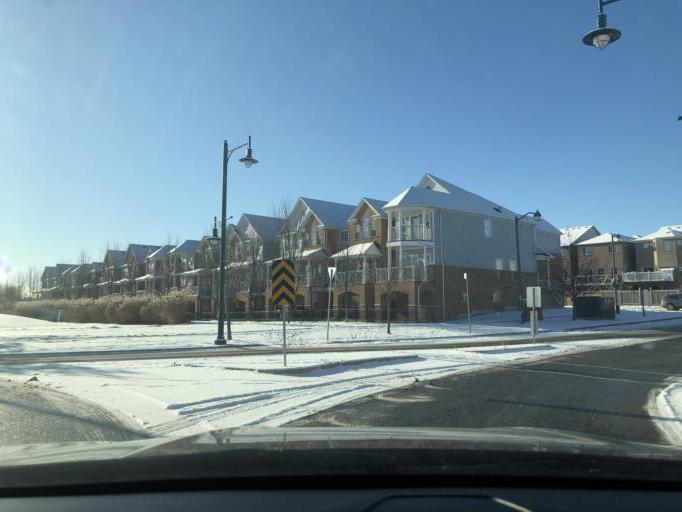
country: CA
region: Ontario
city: Scarborough
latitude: 43.7769
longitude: -79.1356
